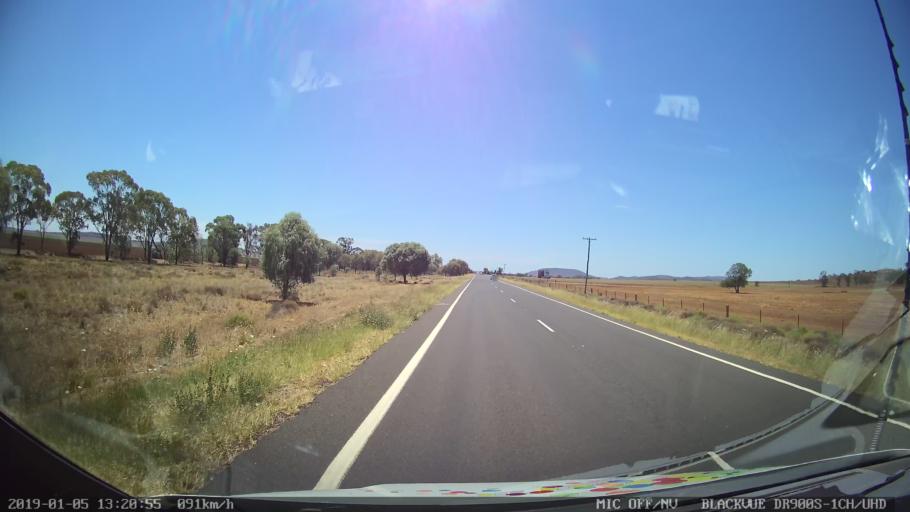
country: AU
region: New South Wales
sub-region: Gunnedah
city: Gunnedah
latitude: -31.0985
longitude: 149.9420
